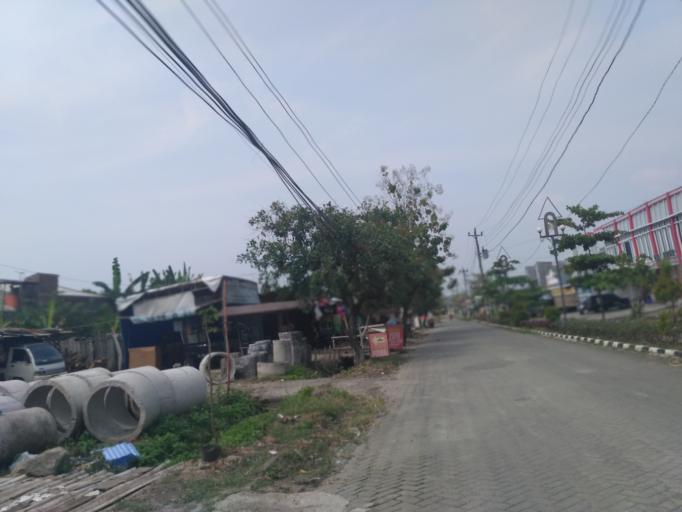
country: ID
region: Central Java
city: Mranggen
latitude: -7.0627
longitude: 110.4629
